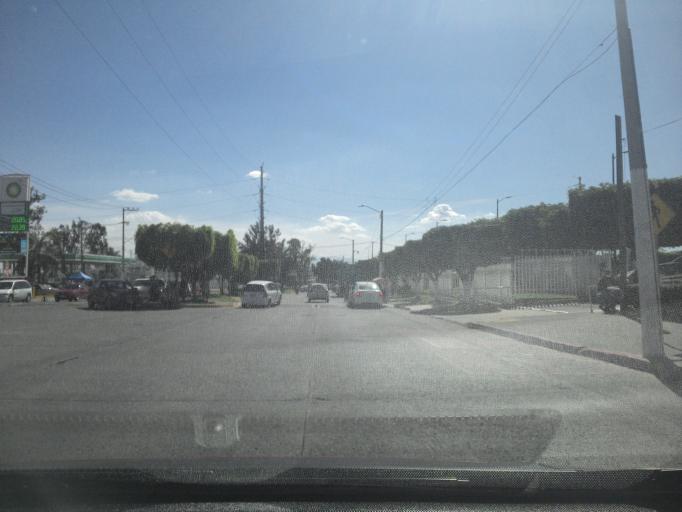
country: MX
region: Jalisco
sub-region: Zapopan
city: Zapopan
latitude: 20.7416
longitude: -103.3996
